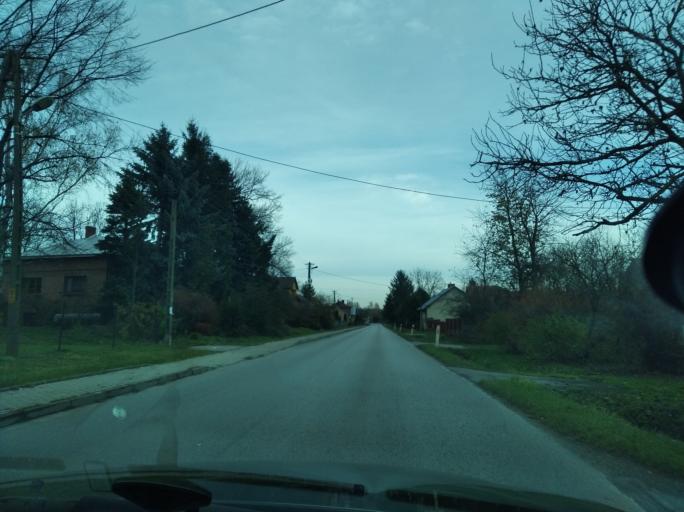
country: PL
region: Subcarpathian Voivodeship
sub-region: Powiat przeworski
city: Przeworsk
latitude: 50.0500
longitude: 22.4682
